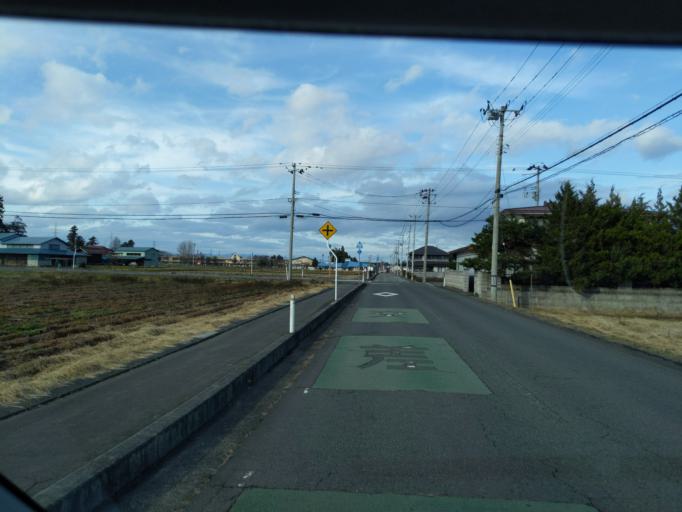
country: JP
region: Iwate
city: Mizusawa
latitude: 39.1350
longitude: 141.0904
